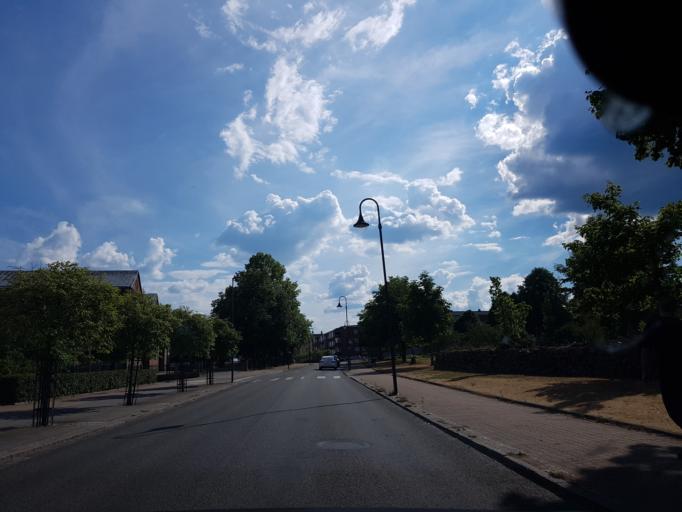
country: SE
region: Joenkoeping
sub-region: Gislaveds Kommun
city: Gislaved
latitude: 57.3051
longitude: 13.5400
